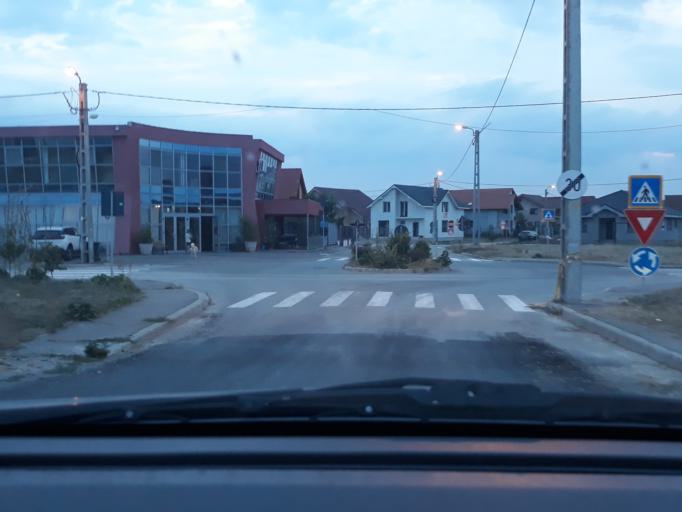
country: RO
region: Bihor
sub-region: Comuna Biharea
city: Oradea
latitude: 47.0259
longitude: 21.9251
